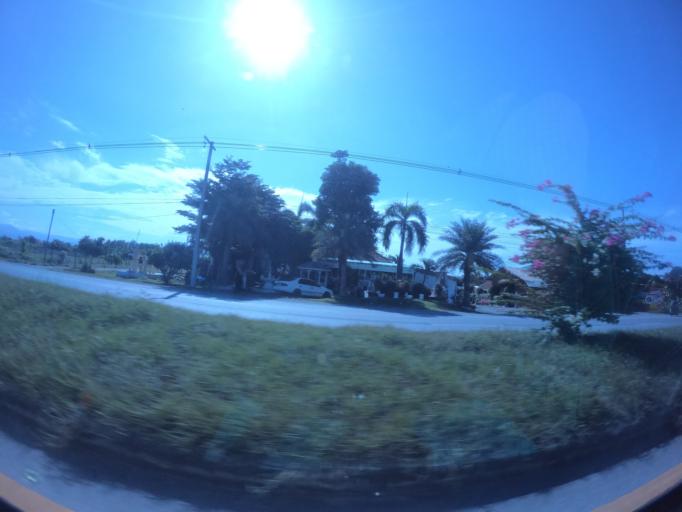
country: TH
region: Nakhon Nayok
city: Ban Na
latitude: 14.2228
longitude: 101.0699
